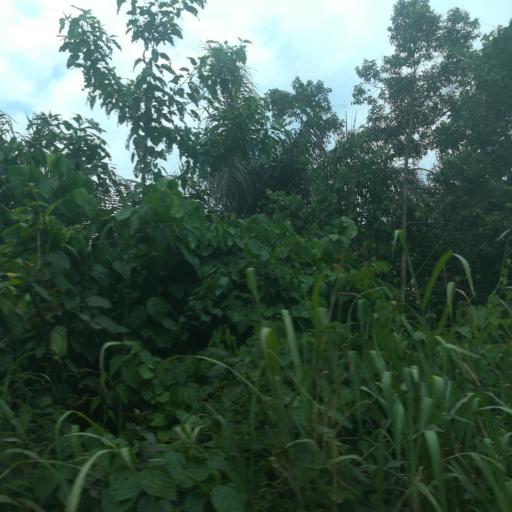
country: NG
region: Lagos
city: Ejirin
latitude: 6.6749
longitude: 3.8004
